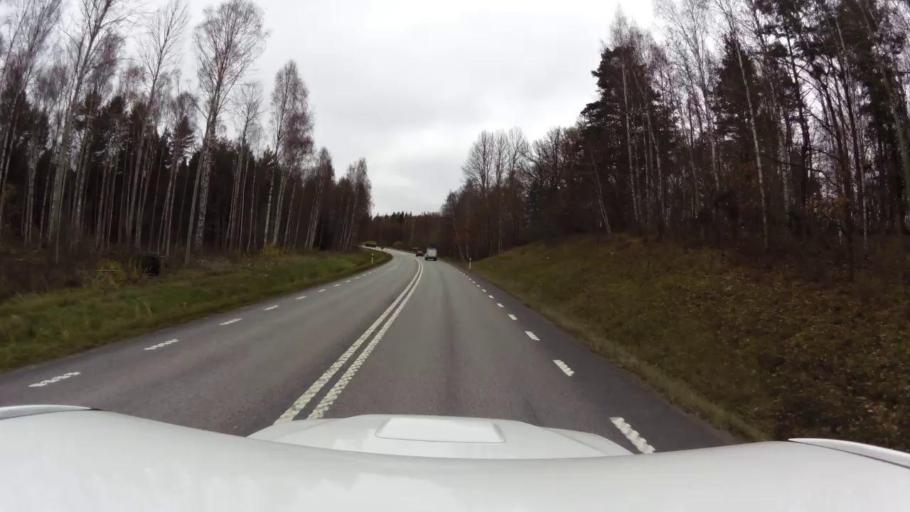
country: SE
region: OEstergoetland
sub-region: Kinda Kommun
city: Rimforsa
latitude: 58.1602
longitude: 15.6813
